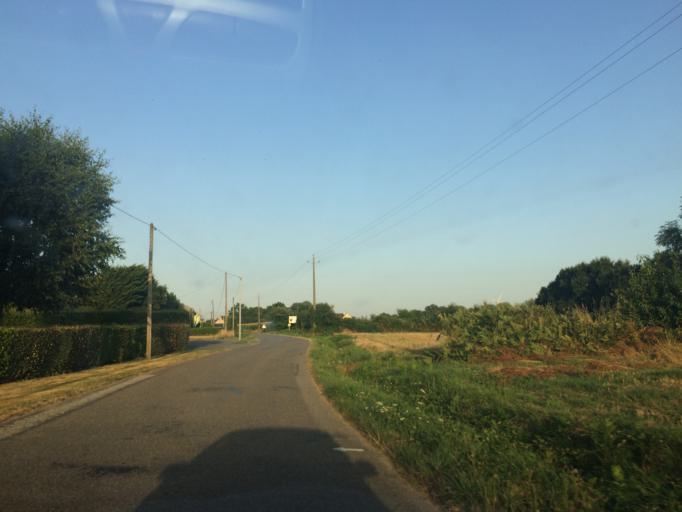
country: FR
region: Brittany
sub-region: Departement du Morbihan
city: Beganne
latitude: 47.6364
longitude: -2.2444
